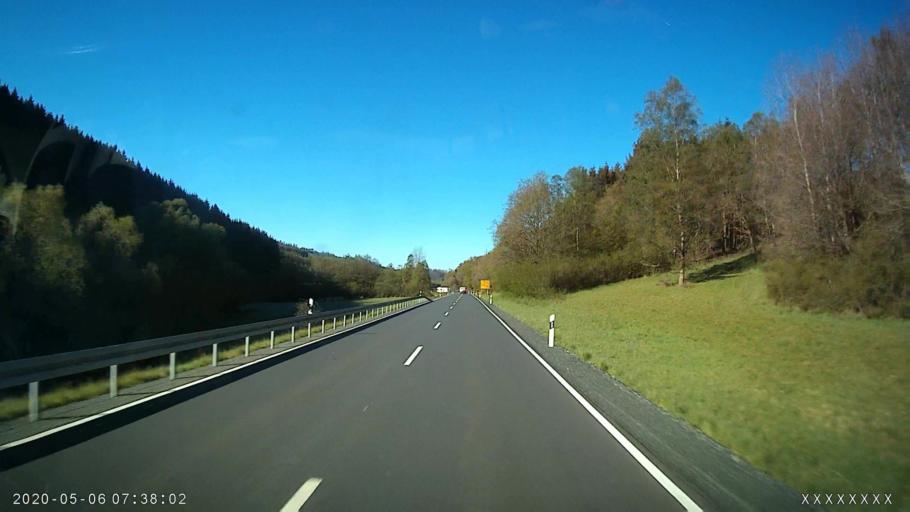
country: DE
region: Hesse
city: Dillenburg
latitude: 50.8043
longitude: 8.2570
